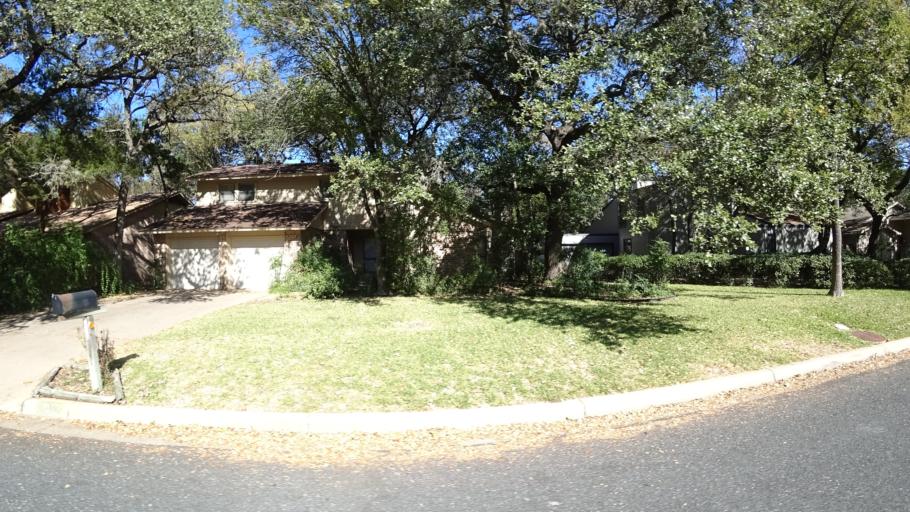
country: US
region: Texas
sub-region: Williamson County
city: Jollyville
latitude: 30.3785
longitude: -97.7515
